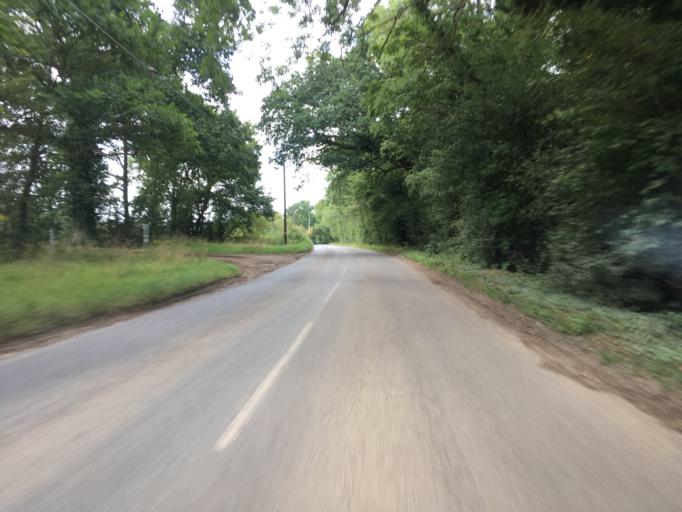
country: GB
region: England
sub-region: Hampshire
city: Overton
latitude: 51.2296
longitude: -1.2608
